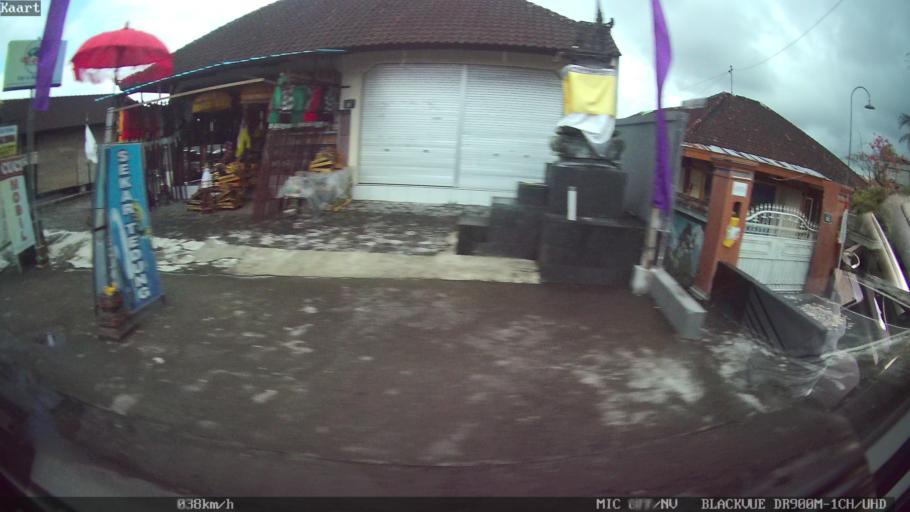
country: ID
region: Bali
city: Banjar Keraman
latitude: -8.5394
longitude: 115.2143
